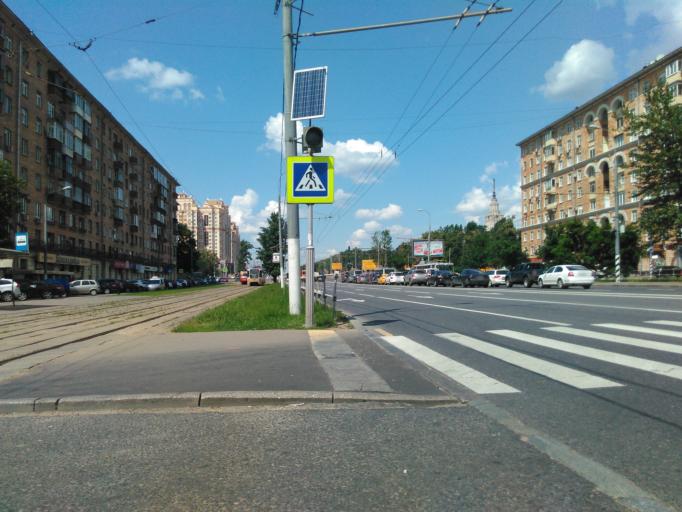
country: RU
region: Moskovskaya
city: Semenovskoye
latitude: 55.6910
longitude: 37.5399
